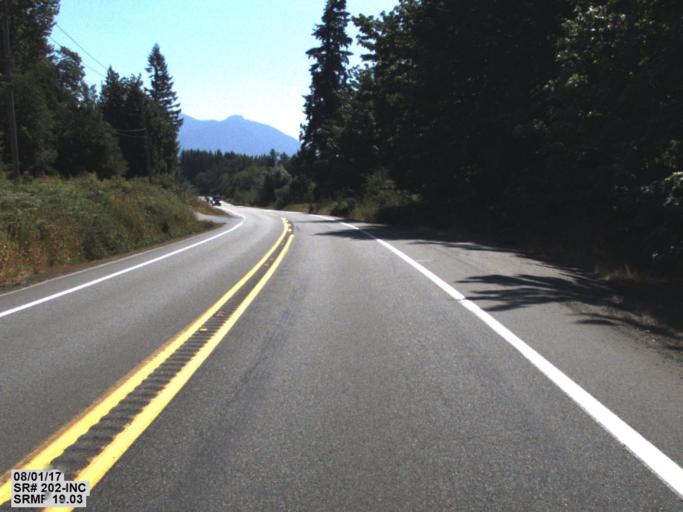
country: US
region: Washington
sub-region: King County
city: Fall City
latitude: 47.5810
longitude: -121.9399
